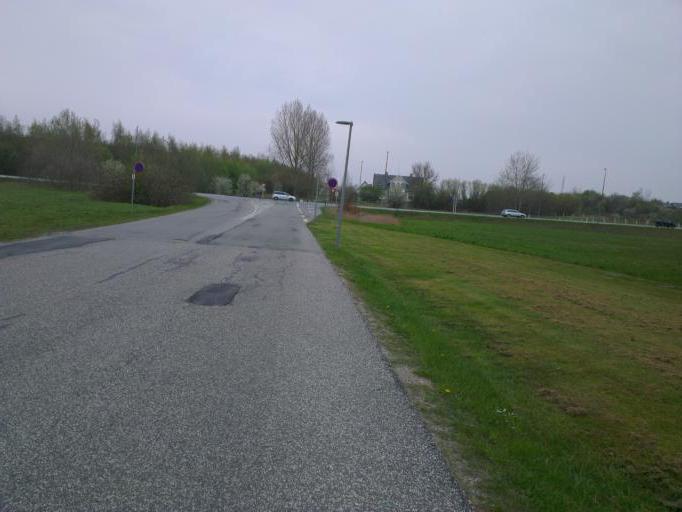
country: DK
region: Capital Region
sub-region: Frederikssund Kommune
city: Frederikssund
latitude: 55.8453
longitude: 12.0828
